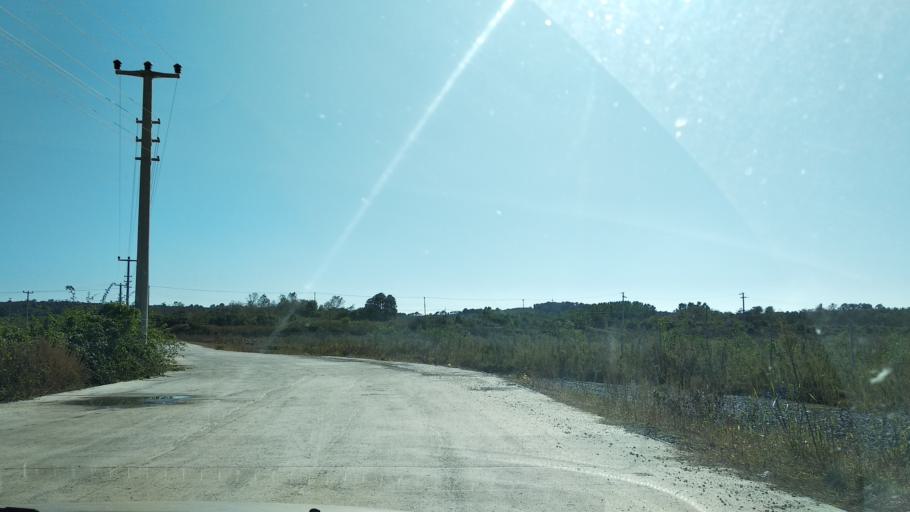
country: TR
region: Sakarya
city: Karasu
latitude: 41.1211
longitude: 30.6078
